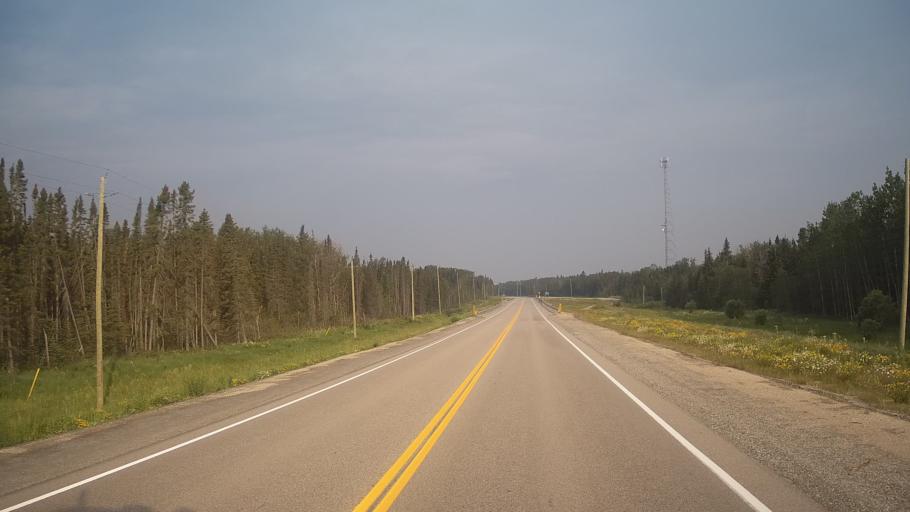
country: CA
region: Ontario
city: Hearst
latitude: 49.7388
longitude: -83.9569
